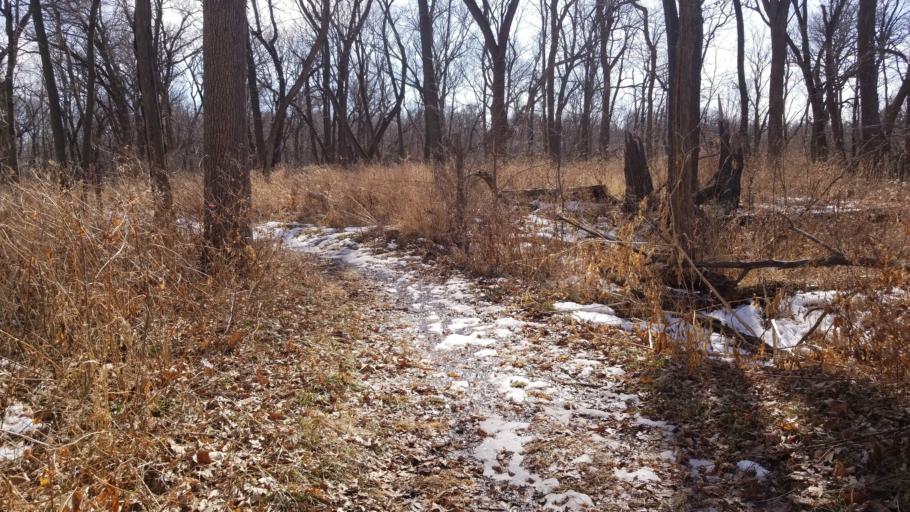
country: US
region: Nebraska
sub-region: Sarpy County
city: Bellevue
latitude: 41.1743
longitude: -95.9019
